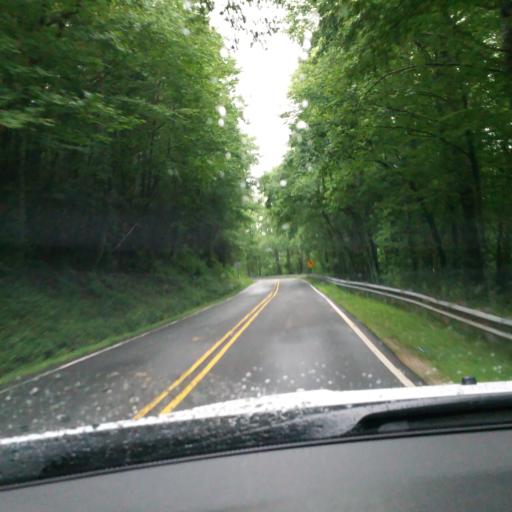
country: US
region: North Carolina
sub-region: Mitchell County
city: Spruce Pine
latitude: 35.7736
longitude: -82.1750
